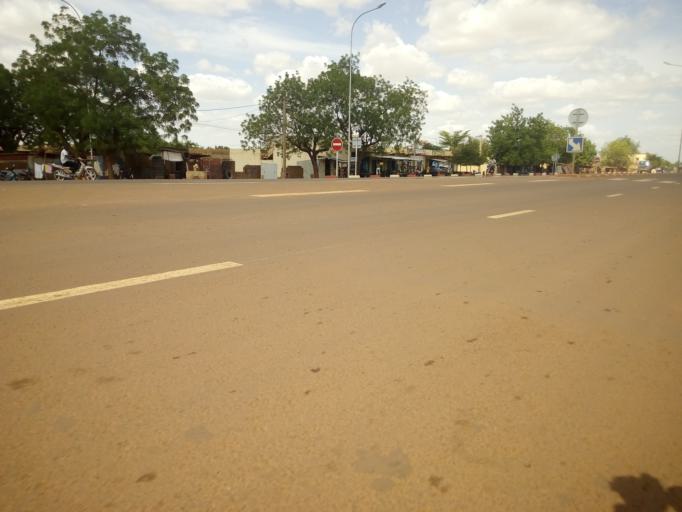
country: ML
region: Segou
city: Segou
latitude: 13.4293
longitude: -6.2230
